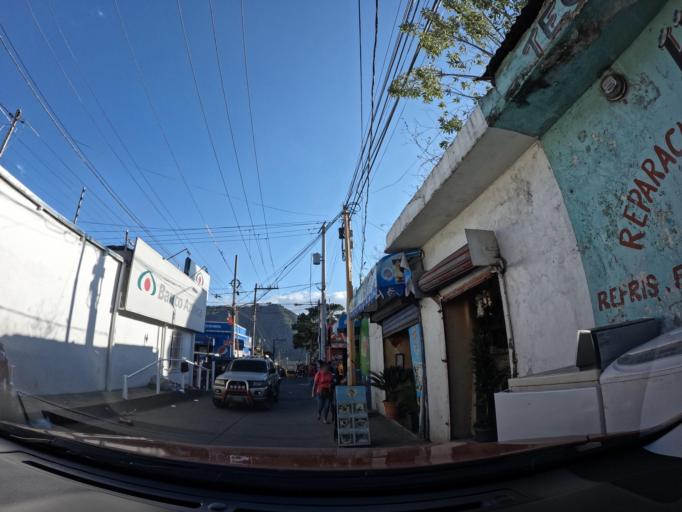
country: GT
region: Escuintla
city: Palin
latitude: 14.4044
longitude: -90.6975
